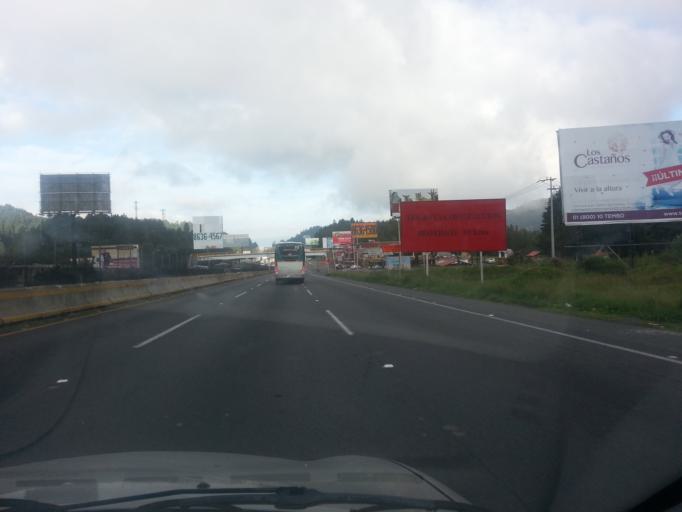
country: MX
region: Mexico
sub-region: Huixquilucan
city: El Palacio
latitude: 19.3018
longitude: -99.3710
